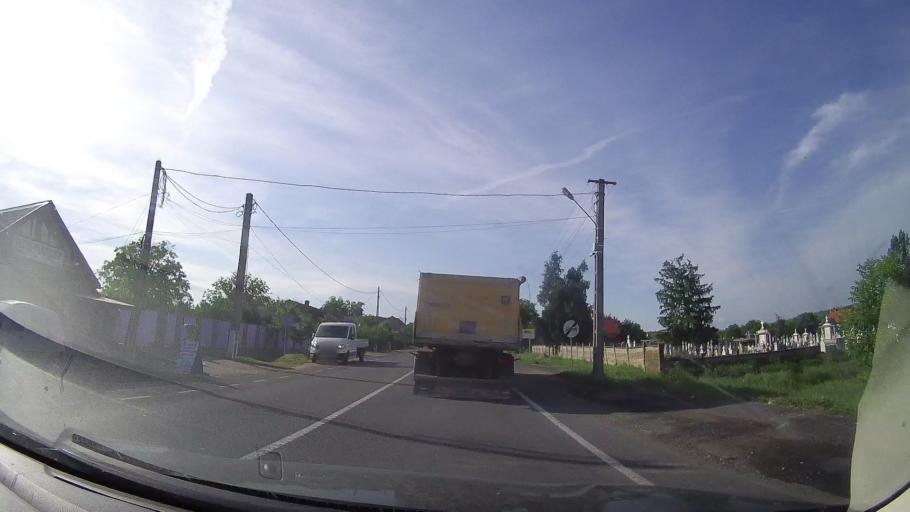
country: RO
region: Timis
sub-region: Comuna Costeiu
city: Costeiu
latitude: 45.7283
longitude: 21.8698
